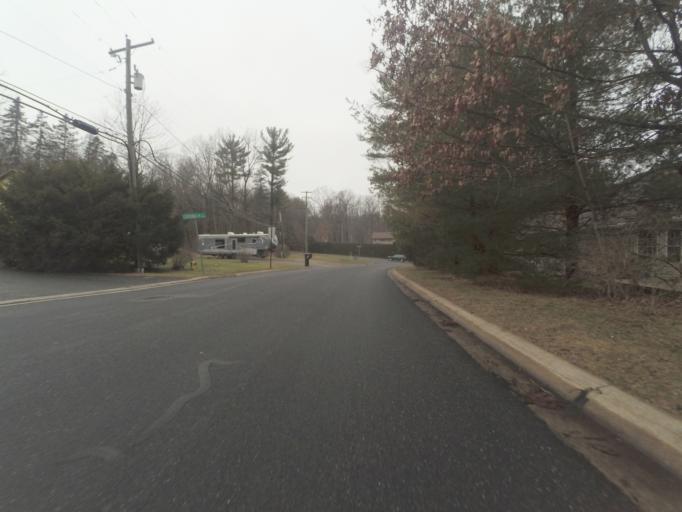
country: US
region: Pennsylvania
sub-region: Centre County
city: Park Forest Village
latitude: 40.7923
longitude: -77.9110
